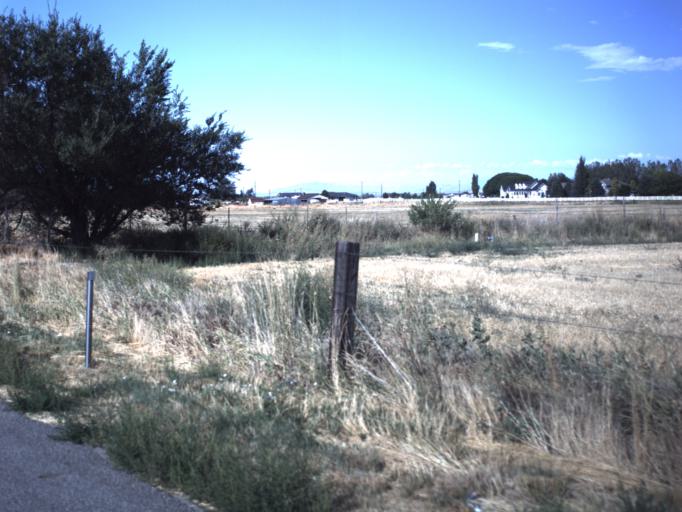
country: US
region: Utah
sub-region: Tooele County
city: Grantsville
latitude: 40.5954
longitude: -112.4258
